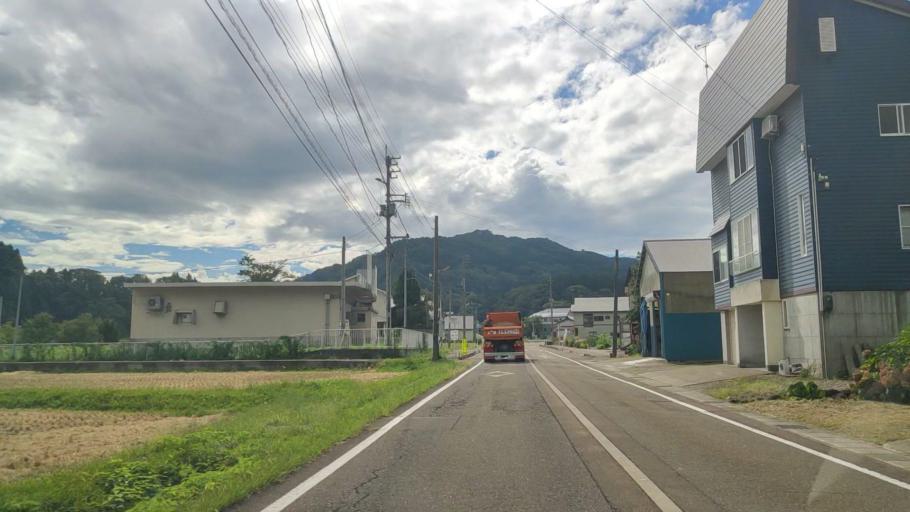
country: JP
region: Niigata
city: Arai
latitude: 36.9610
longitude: 138.2707
